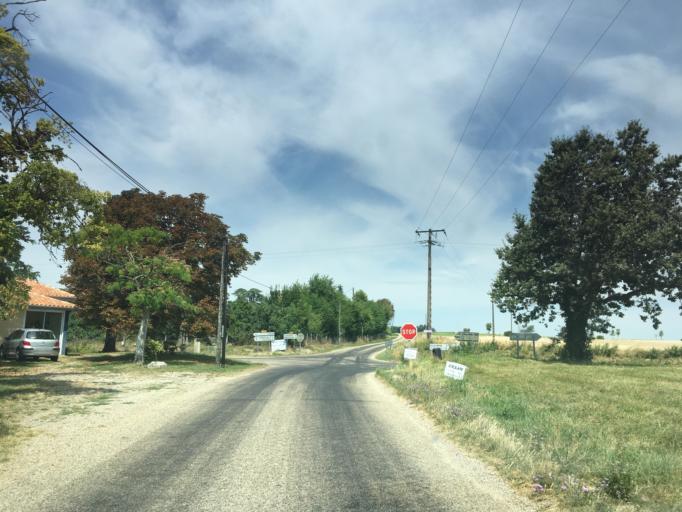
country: FR
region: Midi-Pyrenees
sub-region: Departement du Gers
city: Jegun
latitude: 43.8099
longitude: 0.5029
